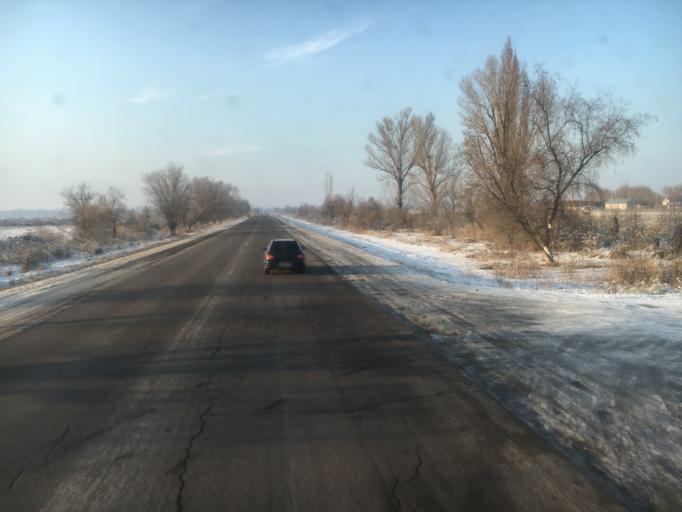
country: KZ
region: Almaty Oblysy
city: Burunday
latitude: 43.3441
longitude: 76.6557
